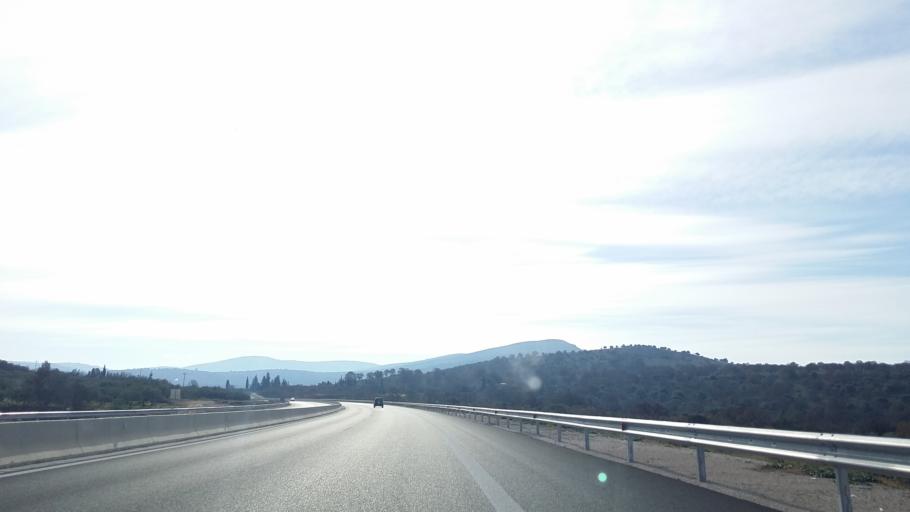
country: GR
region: West Greece
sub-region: Nomos Aitolias kai Akarnanias
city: Sardinia
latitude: 38.8963
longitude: 21.1837
